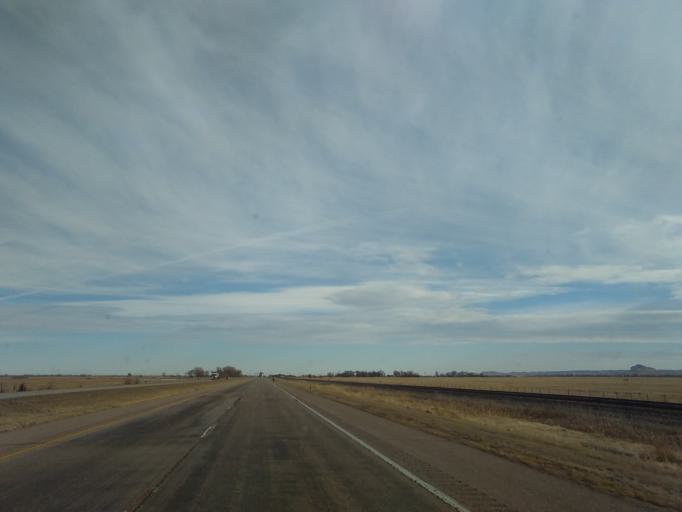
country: US
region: Nebraska
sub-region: Scotts Bluff County
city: Gering
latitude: 41.8247
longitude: -103.5567
